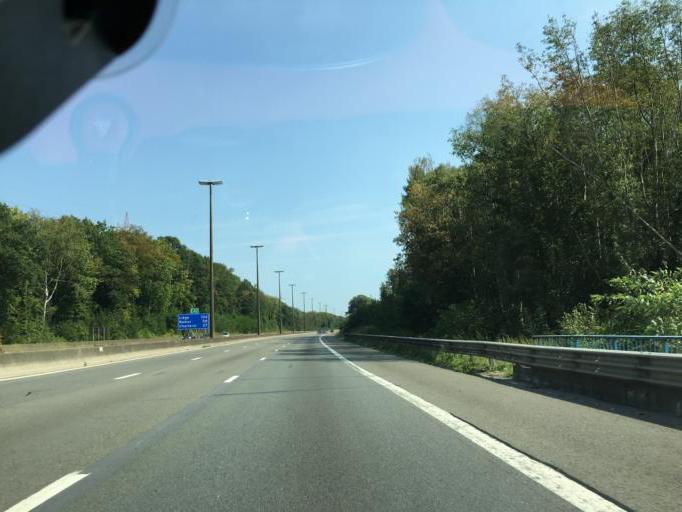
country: BE
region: Wallonia
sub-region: Province du Hainaut
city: Manage
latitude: 50.4973
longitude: 4.2457
